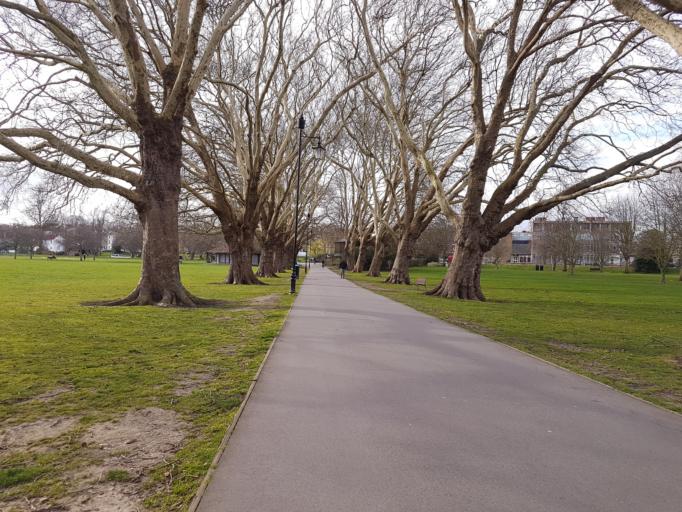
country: GB
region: England
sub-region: Cambridgeshire
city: Cambridge
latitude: 52.2120
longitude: 0.1229
